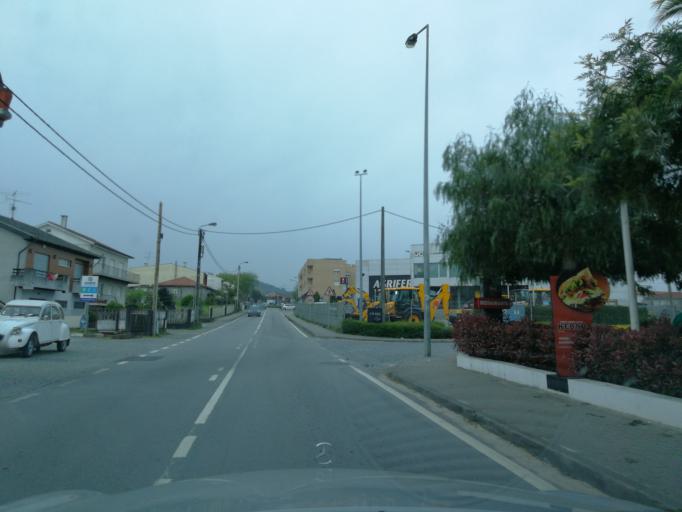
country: PT
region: Braga
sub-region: Braga
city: Braga
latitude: 41.5617
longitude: -8.4444
